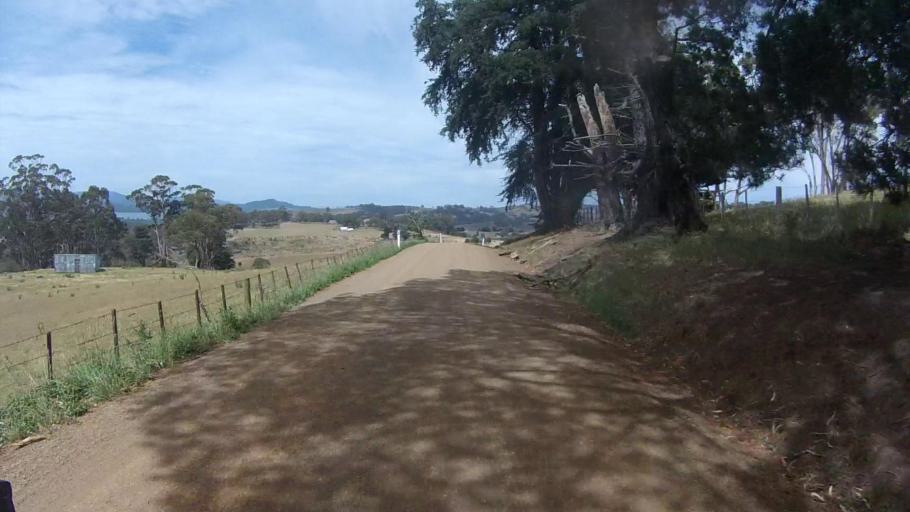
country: AU
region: Tasmania
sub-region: Sorell
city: Sorell
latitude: -42.7950
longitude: 147.8417
